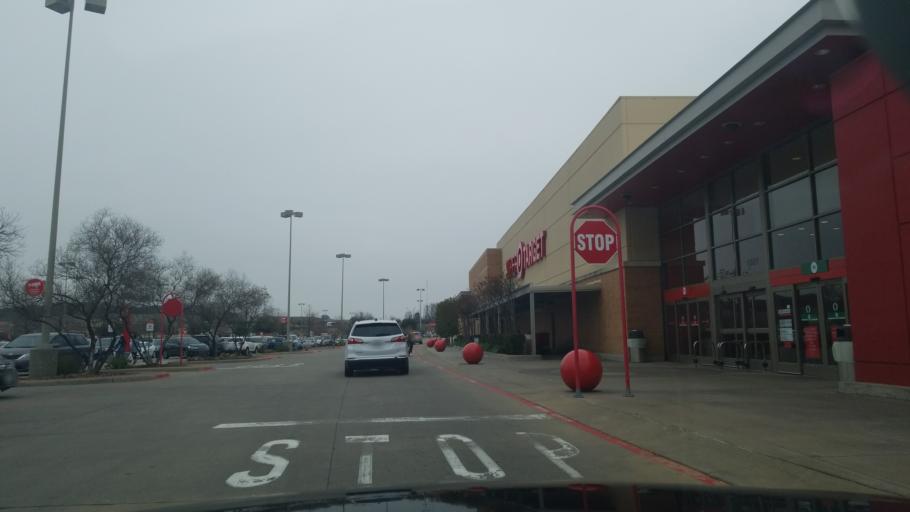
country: US
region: Texas
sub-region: Denton County
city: Denton
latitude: 33.1902
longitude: -97.0989
